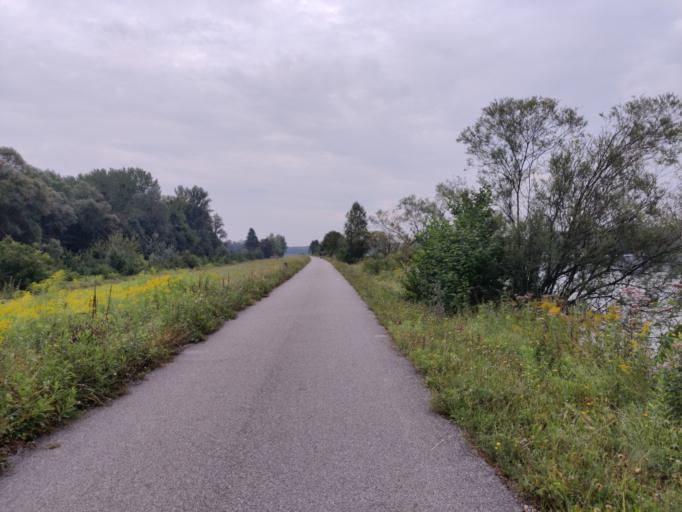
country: AT
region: Upper Austria
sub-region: Politischer Bezirk Urfahr-Umgebung
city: Steyregg
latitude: 48.2627
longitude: 14.3946
